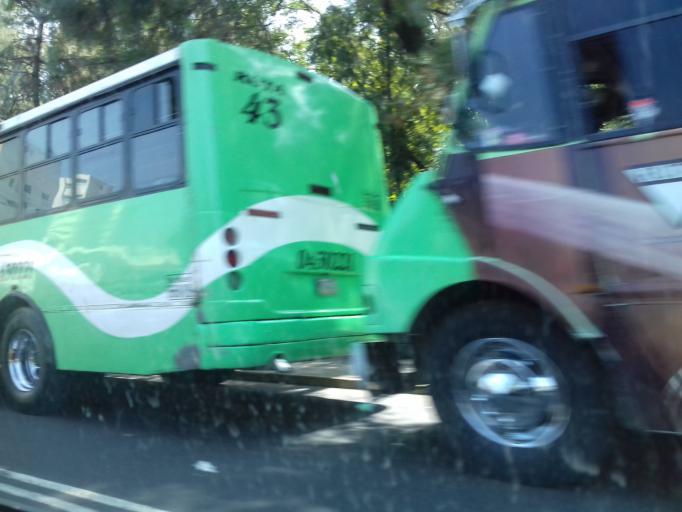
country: MX
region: Mexico City
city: Coyoacan
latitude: 19.3526
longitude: -99.1769
